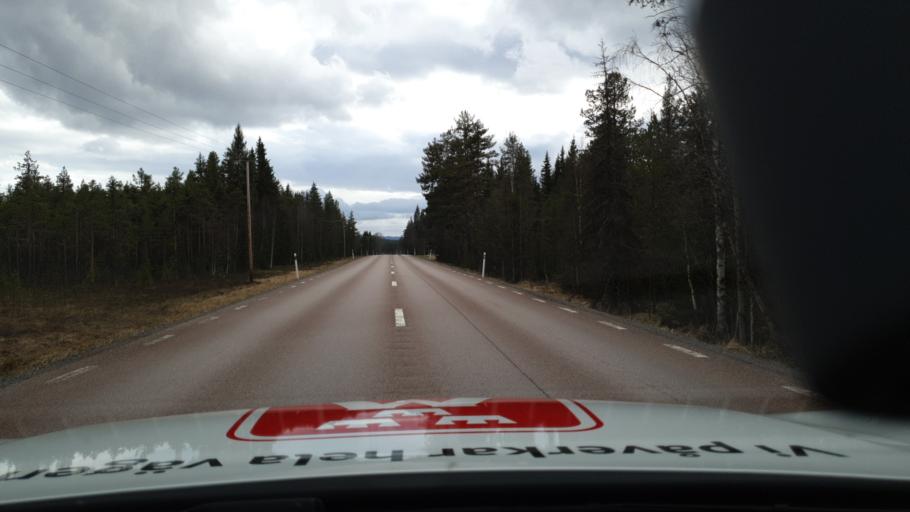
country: SE
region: Jaemtland
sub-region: Ragunda Kommun
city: Hammarstrand
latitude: 63.0252
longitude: 16.7049
